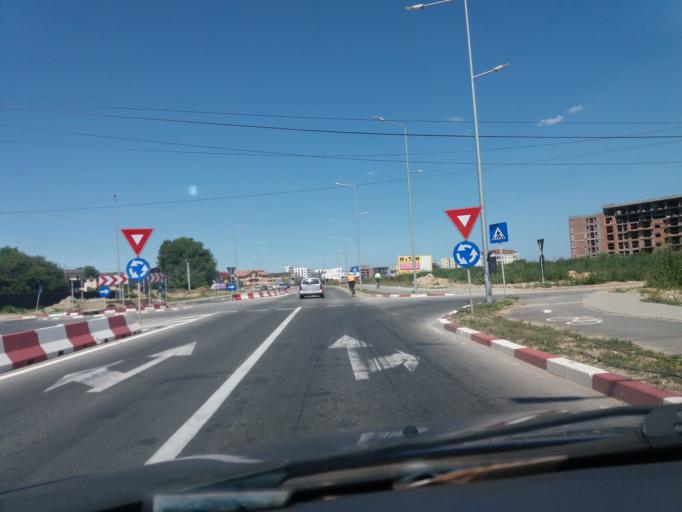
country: RO
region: Constanta
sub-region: Comuna Navodari
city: Navodari
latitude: 44.2889
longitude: 28.6173
